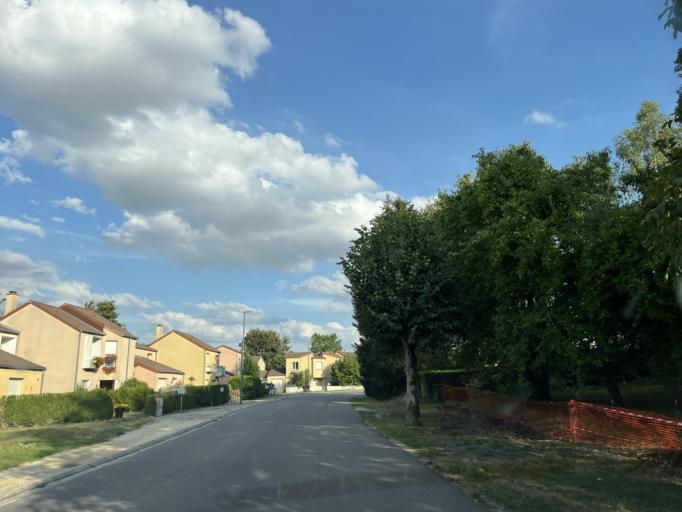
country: FR
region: Lorraine
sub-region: Departement de la Meuse
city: Clermont-en-Argonne
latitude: 49.1059
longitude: 5.0782
